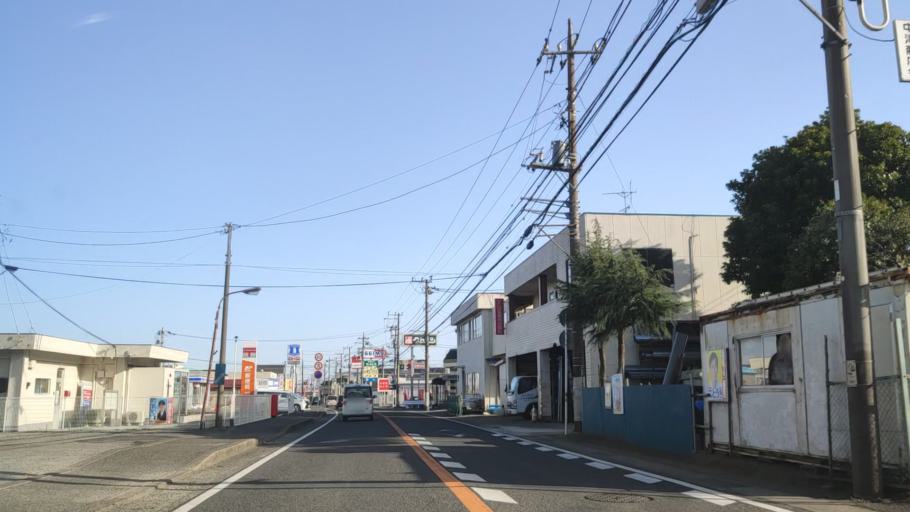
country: JP
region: Kanagawa
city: Zama
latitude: 35.5161
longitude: 139.3344
